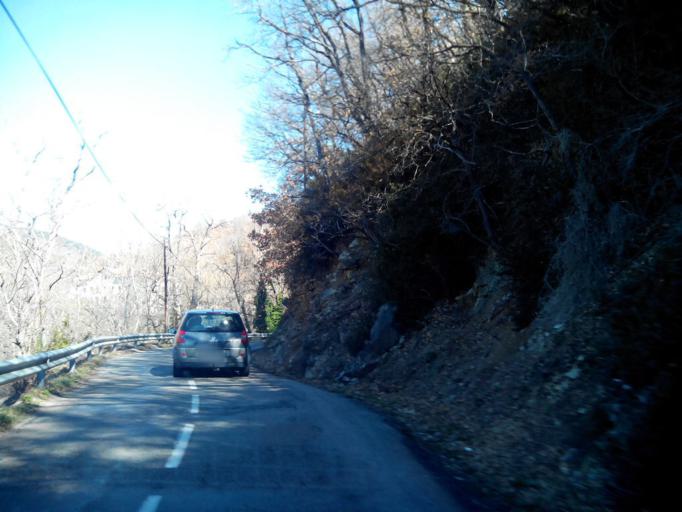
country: ES
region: Catalonia
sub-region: Provincia de Lleida
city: Lles de Cerdanya
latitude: 42.3690
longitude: 1.6834
